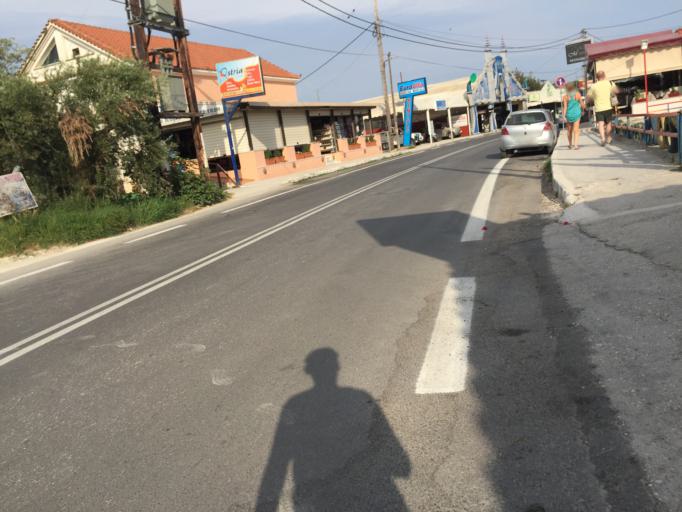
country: GR
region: Ionian Islands
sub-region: Nomos Zakynthou
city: Vanaton
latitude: 37.8153
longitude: 20.8656
